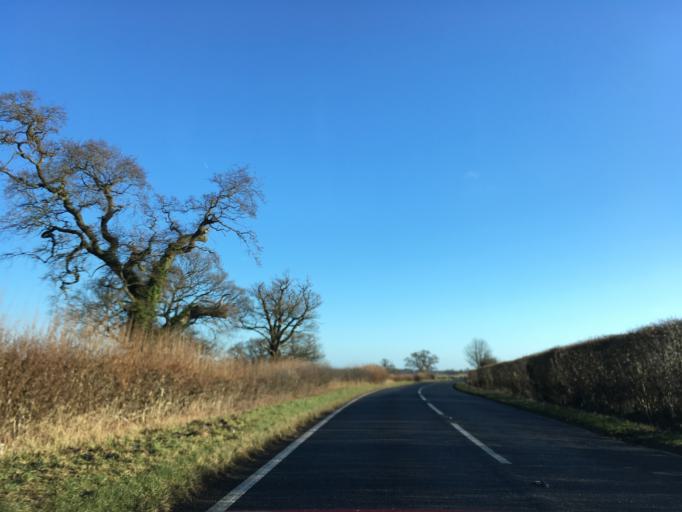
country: GB
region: England
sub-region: Wiltshire
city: Nettleton
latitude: 51.5264
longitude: -2.3018
